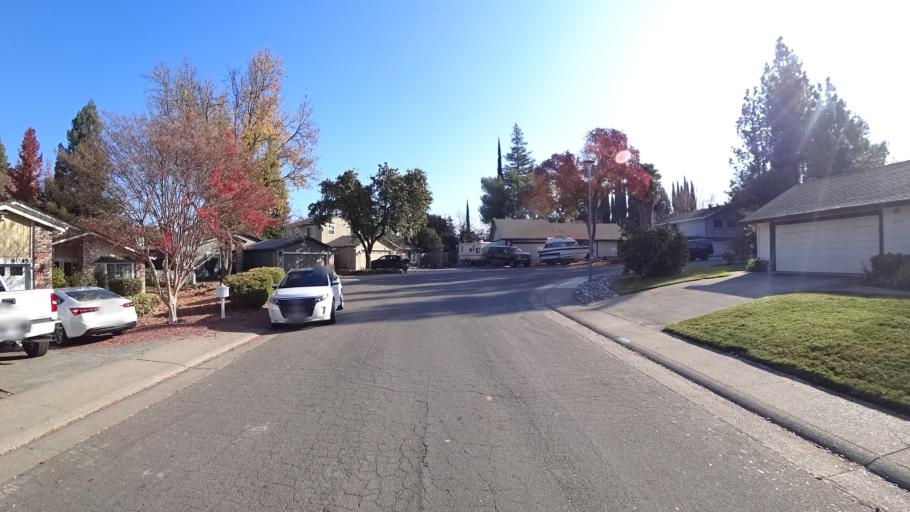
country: US
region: California
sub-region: Sacramento County
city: Citrus Heights
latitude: 38.7142
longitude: -121.2633
